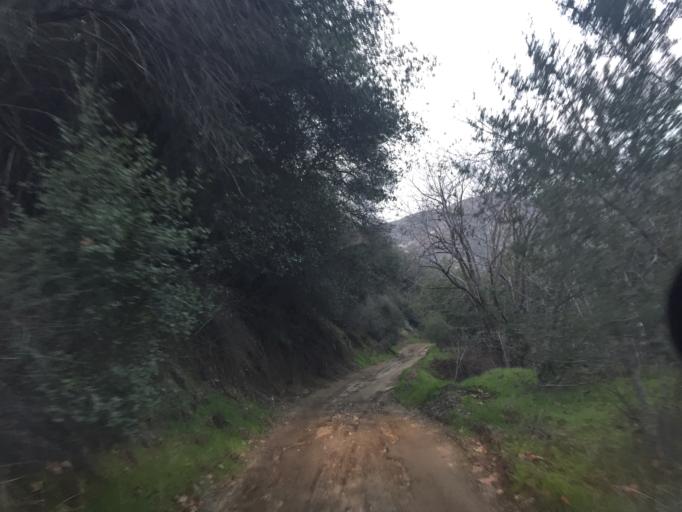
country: US
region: California
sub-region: San Bernardino County
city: Yucaipa
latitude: 34.1164
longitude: -117.0609
